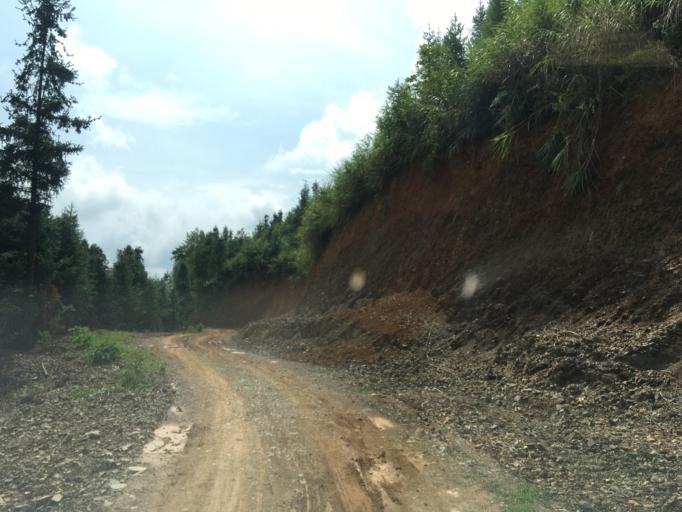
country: CN
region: Guangxi Zhuangzu Zizhiqu
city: Xinzhou
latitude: 24.8675
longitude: 105.8504
